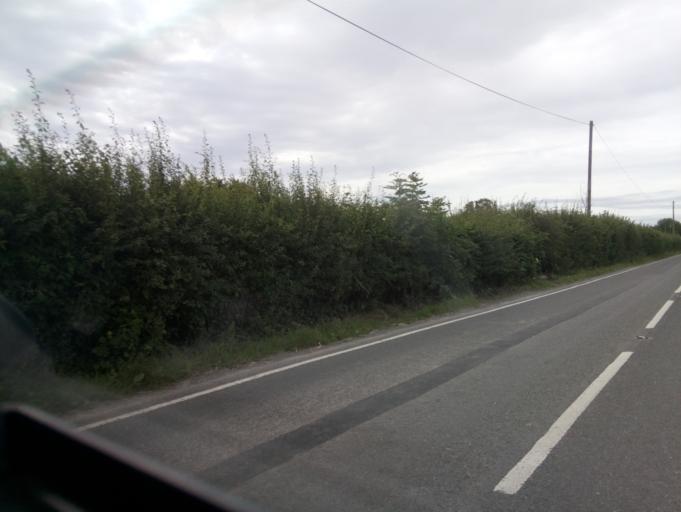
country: GB
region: England
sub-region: North Somerset
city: Churchill
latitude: 51.3557
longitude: -2.7936
